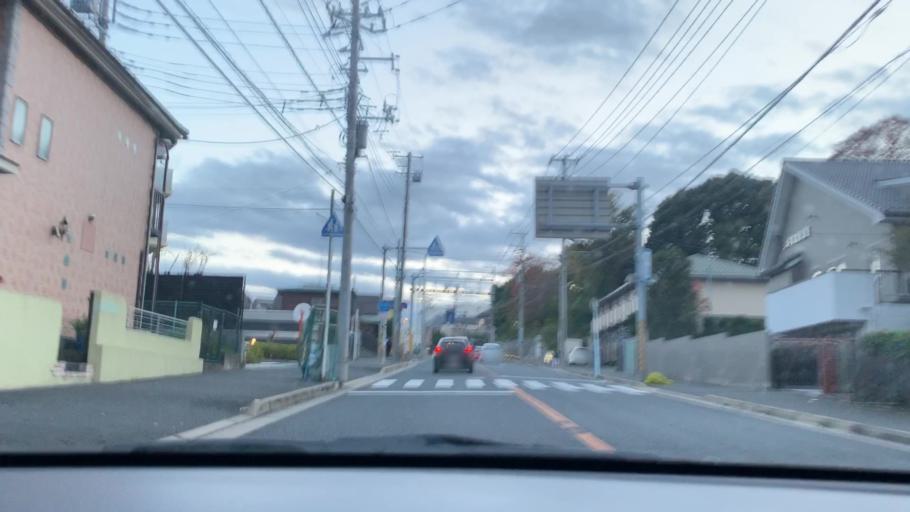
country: JP
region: Chiba
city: Matsudo
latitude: 35.7715
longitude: 139.8973
